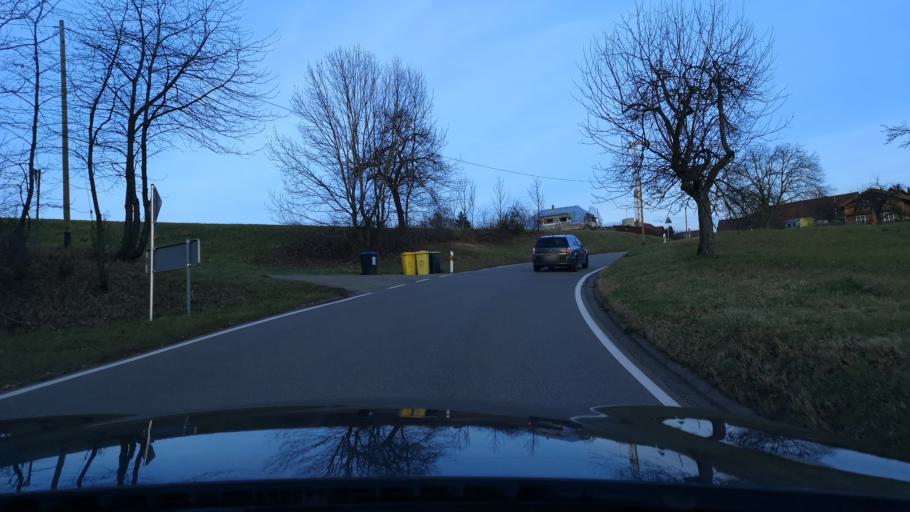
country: DE
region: Baden-Wuerttemberg
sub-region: Regierungsbezirk Stuttgart
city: Rudersberg
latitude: 48.9069
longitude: 9.5289
